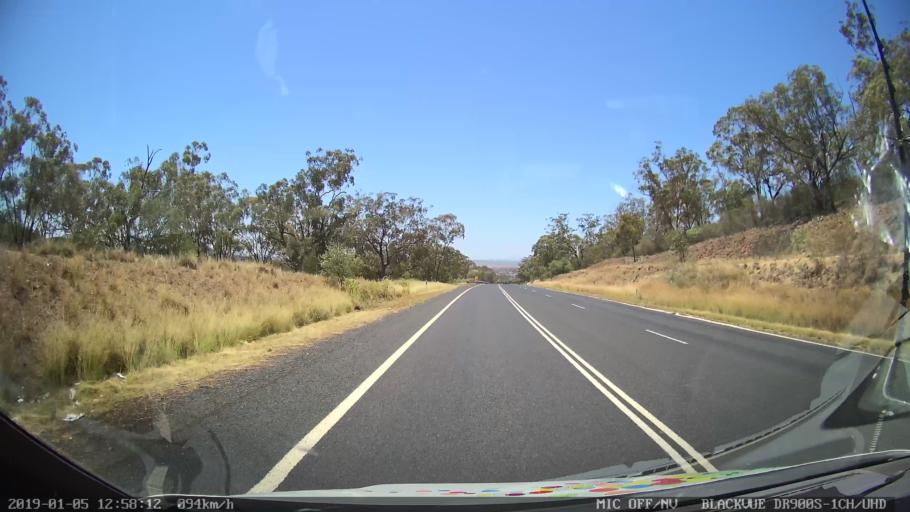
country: AU
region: New South Wales
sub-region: Warrumbungle Shire
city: Coonabarabran
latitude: -31.1110
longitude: 149.7464
